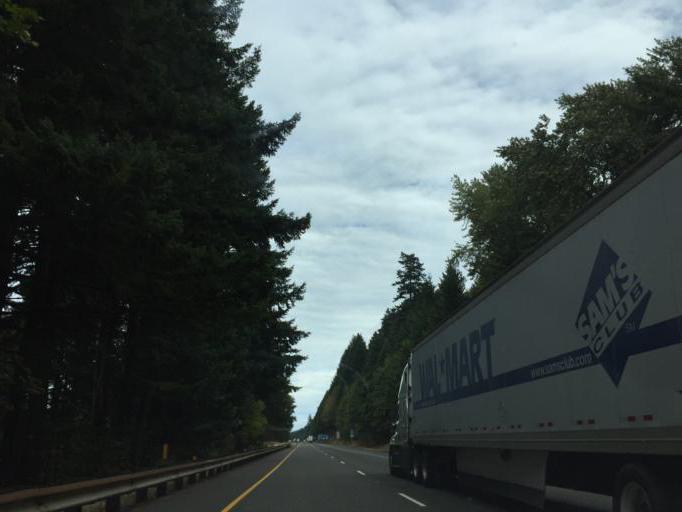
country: US
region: Oregon
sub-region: Hood River County
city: Cascade Locks
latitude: 45.6440
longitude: -121.9248
